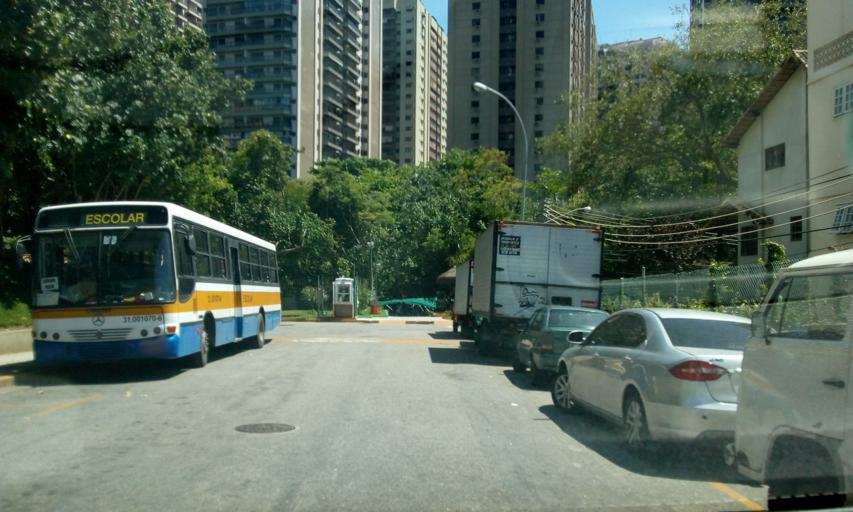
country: BR
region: Rio de Janeiro
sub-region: Rio De Janeiro
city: Rio de Janeiro
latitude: -23.0081
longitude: -43.3273
